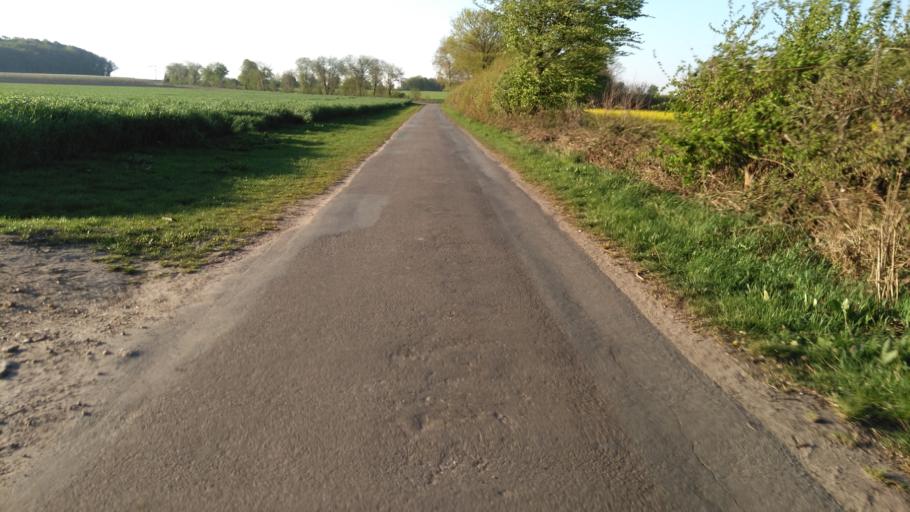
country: DE
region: Lower Saxony
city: Bliedersdorf
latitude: 53.4763
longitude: 9.5781
